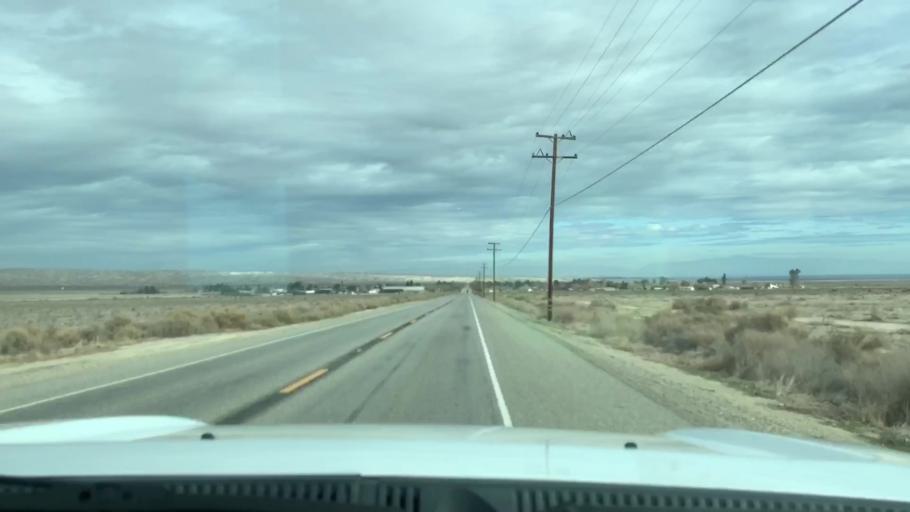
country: US
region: California
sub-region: Kern County
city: Ford City
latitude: 35.1995
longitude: -119.4202
